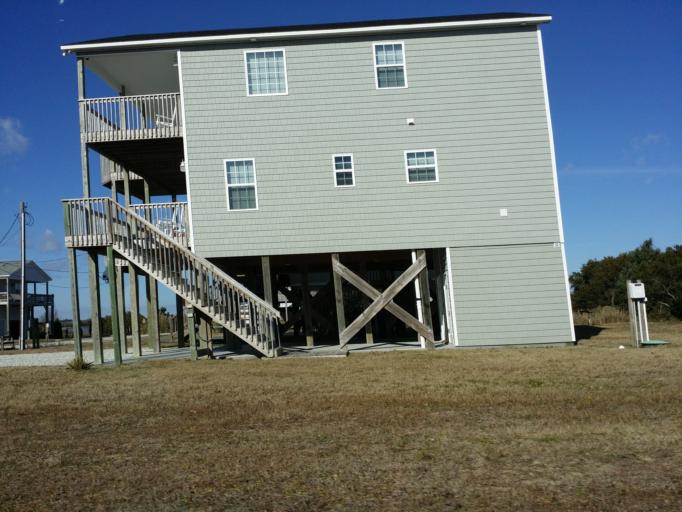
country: US
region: North Carolina
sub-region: Pender County
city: Surf City
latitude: 34.4708
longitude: -77.4672
